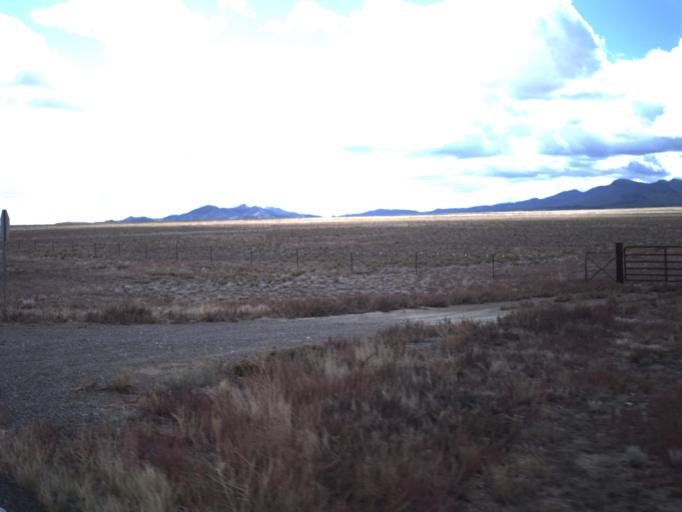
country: US
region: Utah
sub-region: Beaver County
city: Milford
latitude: 38.6522
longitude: -113.8705
